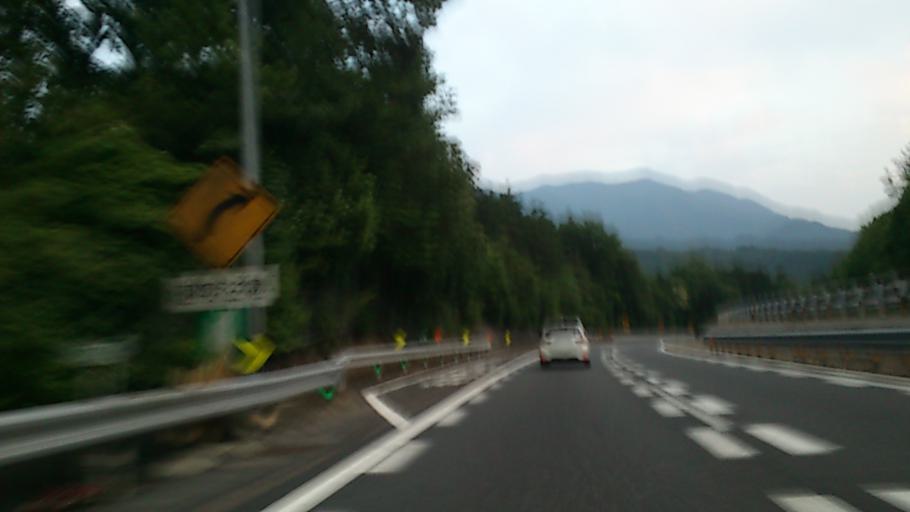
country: JP
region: Gifu
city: Nakatsugawa
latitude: 35.5154
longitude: 137.5617
